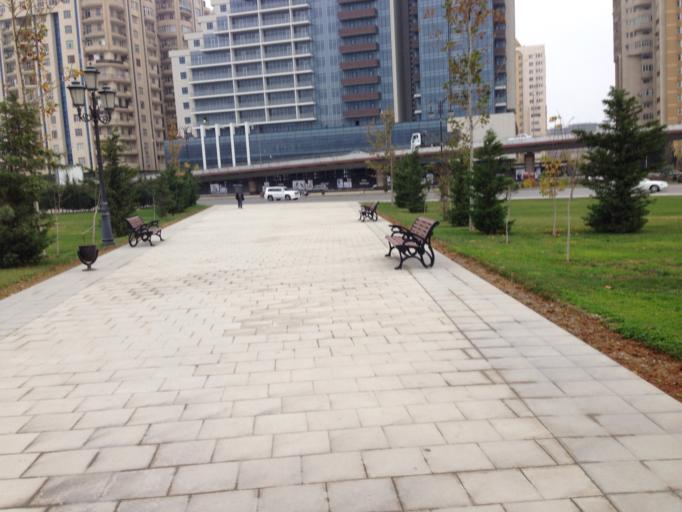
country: AZ
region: Baki
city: Baku
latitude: 40.3896
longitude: 49.8682
